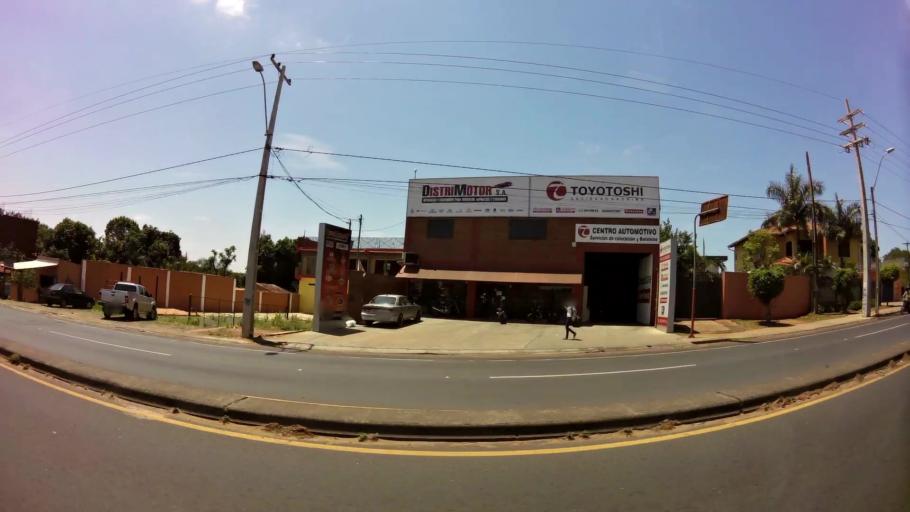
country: PY
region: Central
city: Nemby
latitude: -25.3989
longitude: -57.5442
